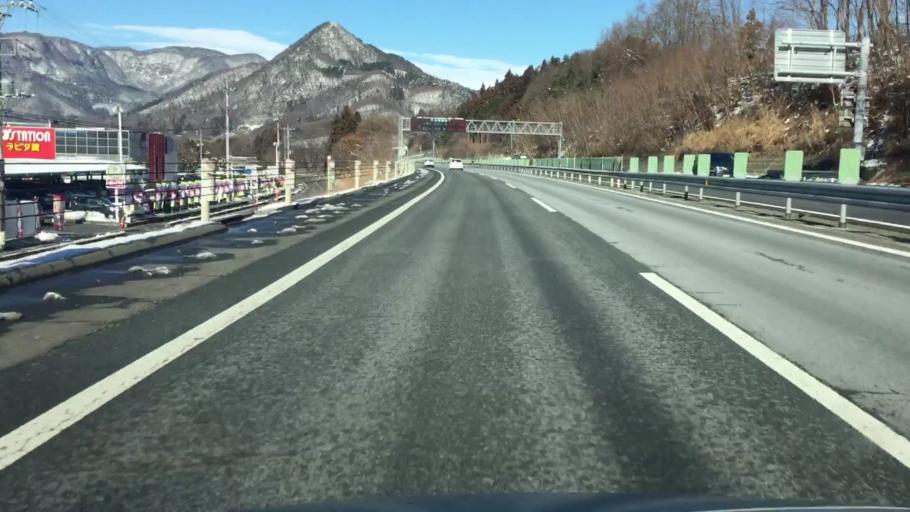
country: JP
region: Gunma
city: Numata
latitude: 36.6633
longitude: 139.0671
